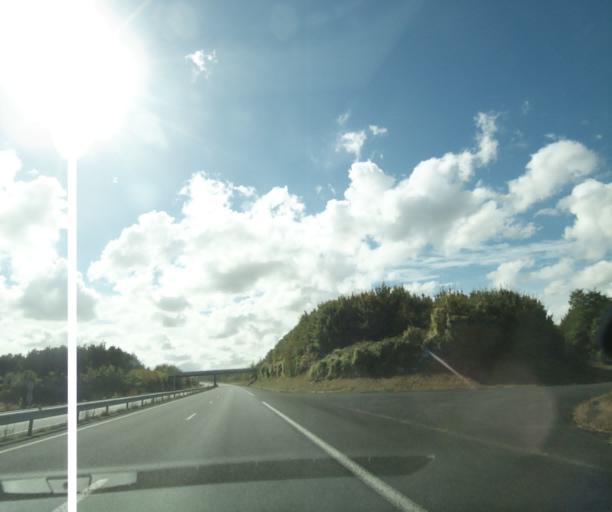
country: FR
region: Poitou-Charentes
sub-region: Departement de la Charente-Maritime
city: Saint-Savinien
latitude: 45.8290
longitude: -0.7093
